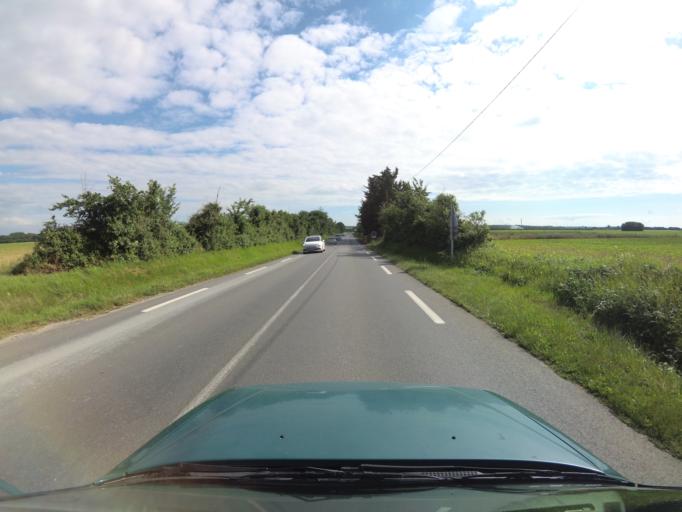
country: FR
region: Poitou-Charentes
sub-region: Departement de la Charente-Maritime
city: Saint-Xandre
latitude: 46.2233
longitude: -1.0849
